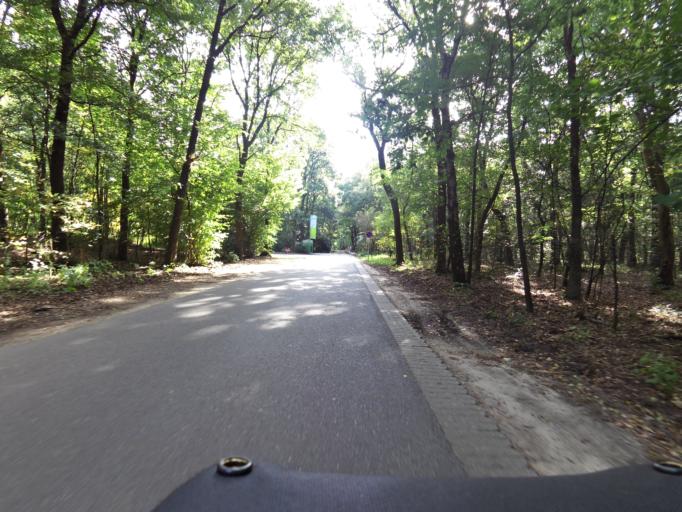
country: NL
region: Gelderland
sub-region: Gemeente Apeldoorn
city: Uddel
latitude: 52.2179
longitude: 5.7838
